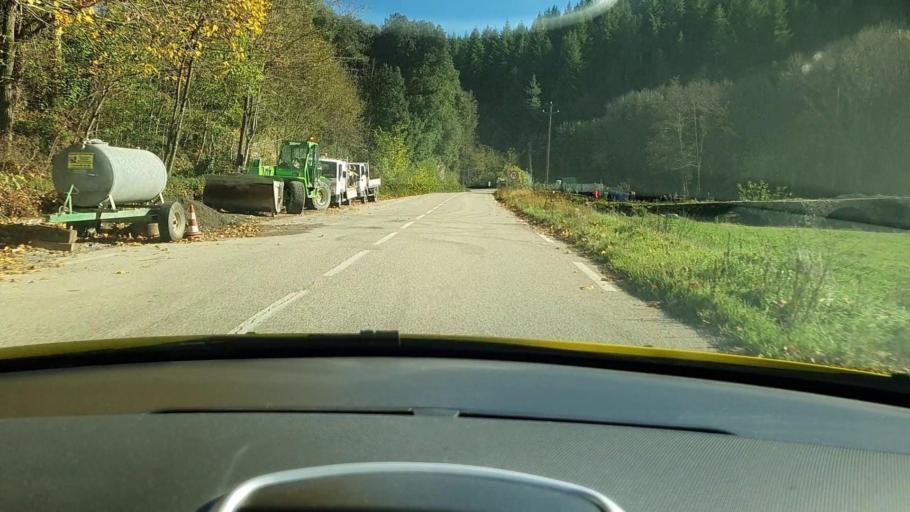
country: FR
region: Languedoc-Roussillon
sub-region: Departement du Gard
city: Valleraugue
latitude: 44.1398
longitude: 3.7200
